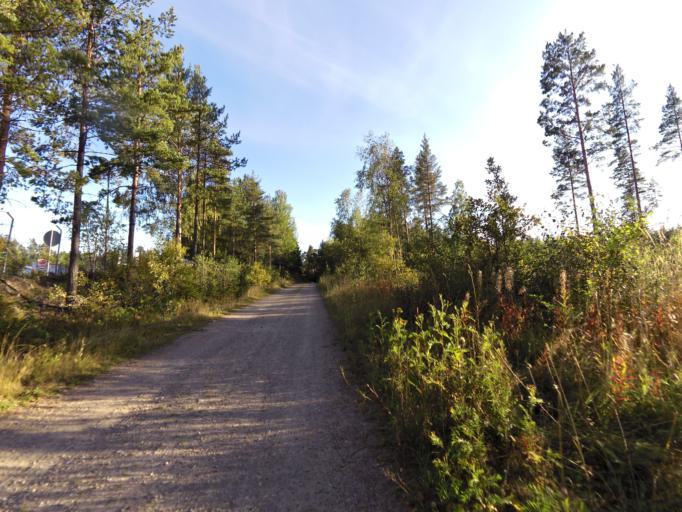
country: SE
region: Gaevleborg
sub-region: Gavle Kommun
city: Gavle
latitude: 60.6492
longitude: 17.1161
